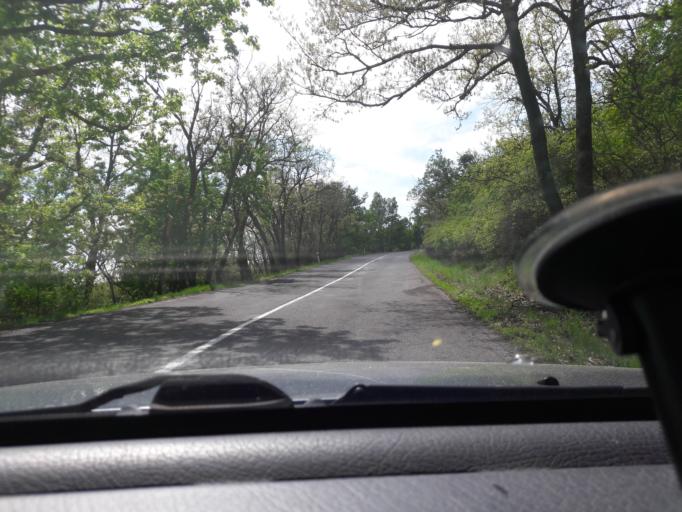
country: SK
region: Banskobystricky
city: Dudince
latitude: 48.2639
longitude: 18.8422
